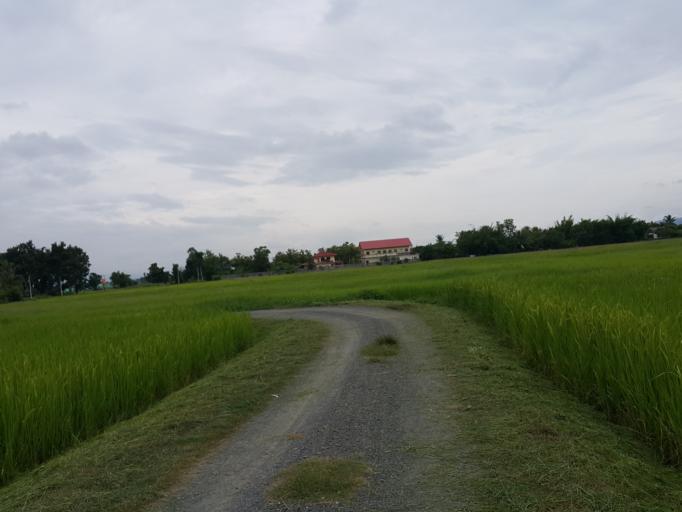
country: TH
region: Chiang Mai
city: San Sai
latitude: 18.8542
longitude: 99.1165
